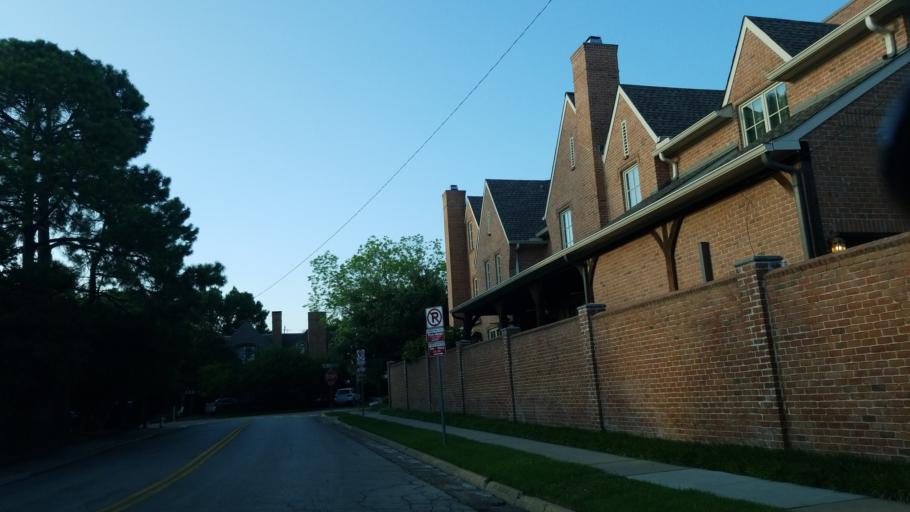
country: US
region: Texas
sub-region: Dallas County
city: Highland Park
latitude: 32.8423
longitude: -96.7919
